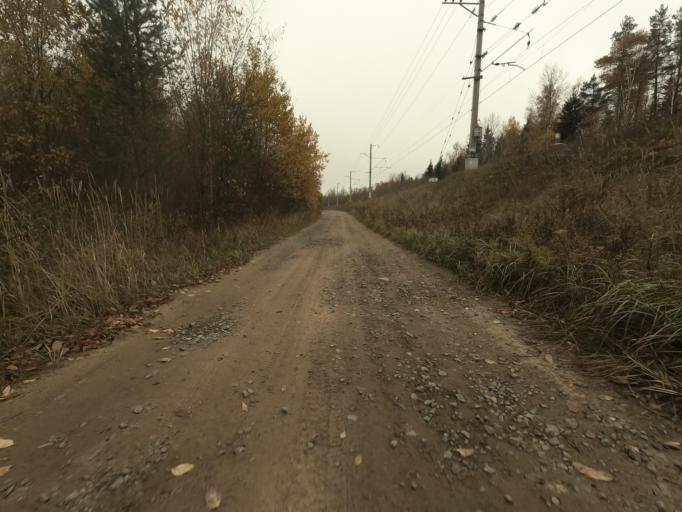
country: RU
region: Leningrad
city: Pavlovo
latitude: 59.7818
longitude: 30.8960
